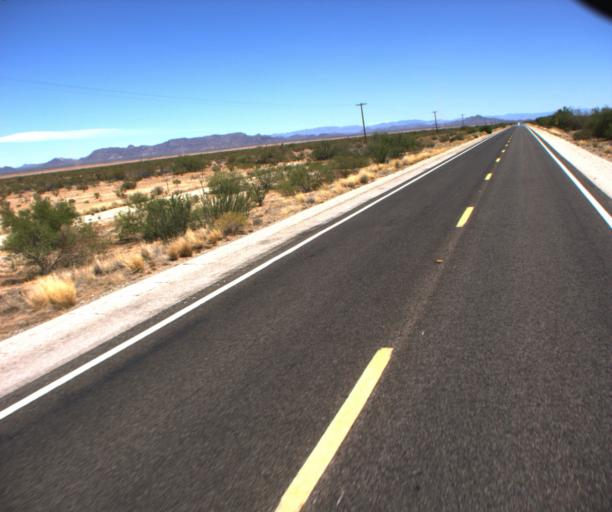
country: US
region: Arizona
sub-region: La Paz County
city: Salome
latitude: 33.9207
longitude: -113.2470
